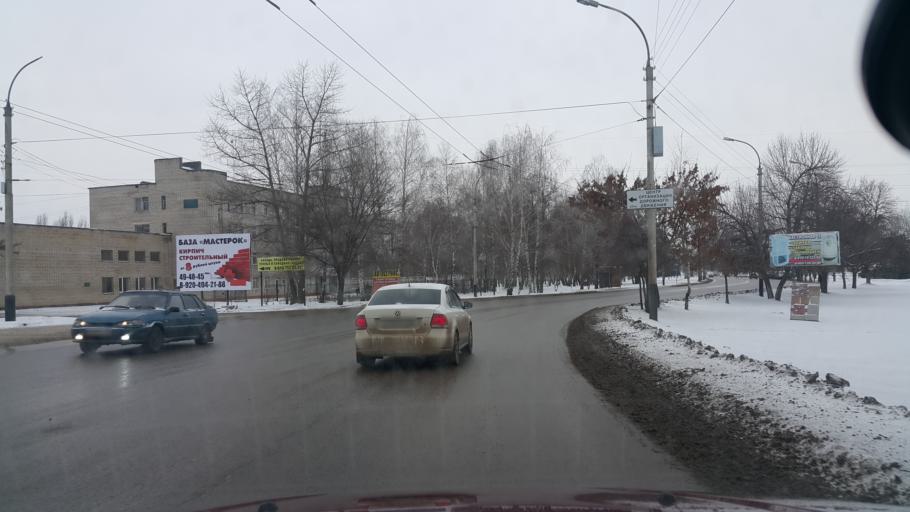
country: RU
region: Tambov
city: Tambov
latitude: 52.7357
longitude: 41.3889
